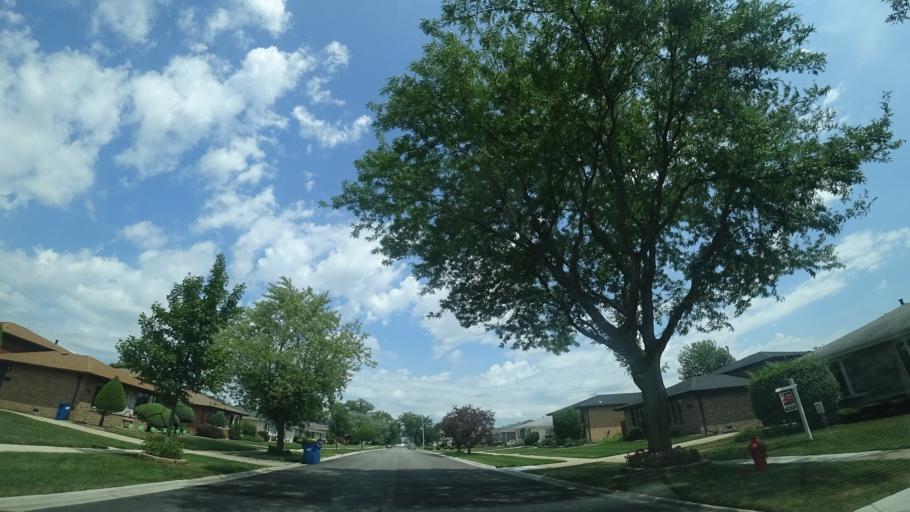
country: US
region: Illinois
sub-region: Cook County
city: Alsip
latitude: 41.6725
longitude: -87.7461
